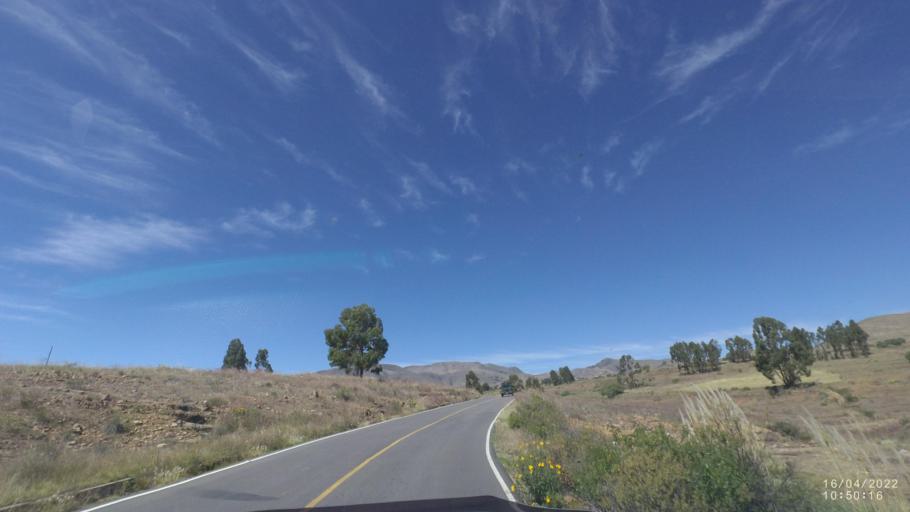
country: BO
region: Cochabamba
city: Arani
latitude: -17.7933
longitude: -65.8039
